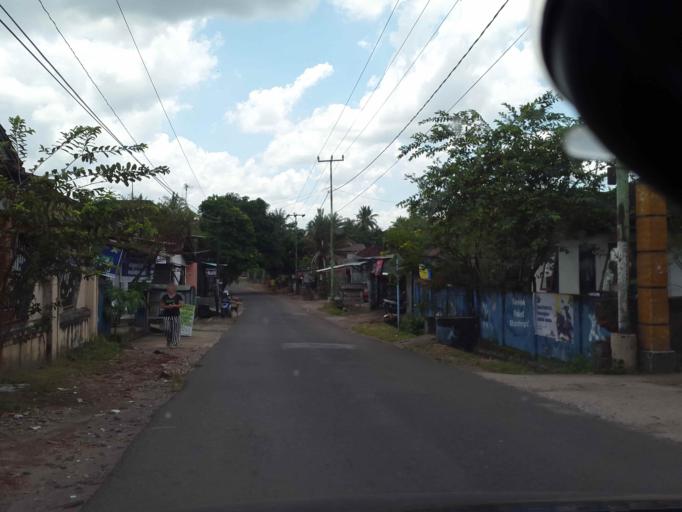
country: ID
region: West Nusa Tenggara
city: Mambalan
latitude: -8.5384
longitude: 116.0941
